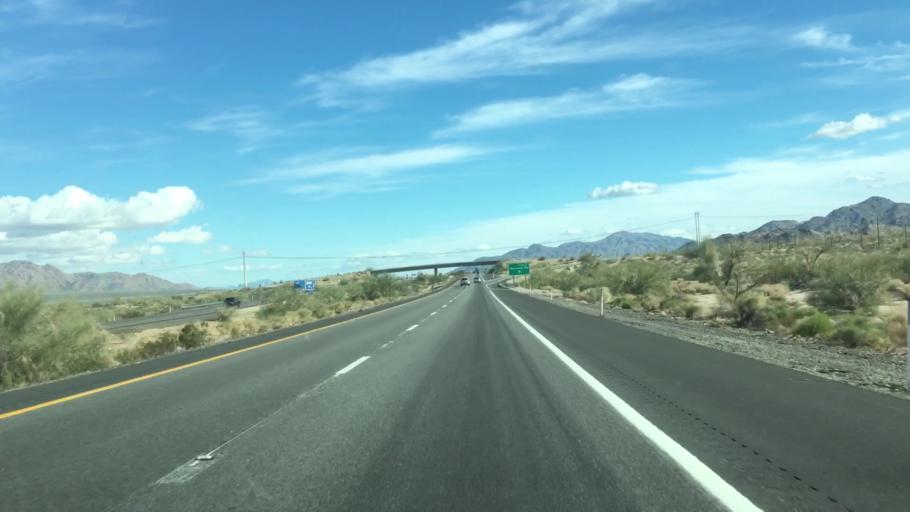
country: US
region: California
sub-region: Riverside County
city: Mecca
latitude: 33.6677
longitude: -115.6597
